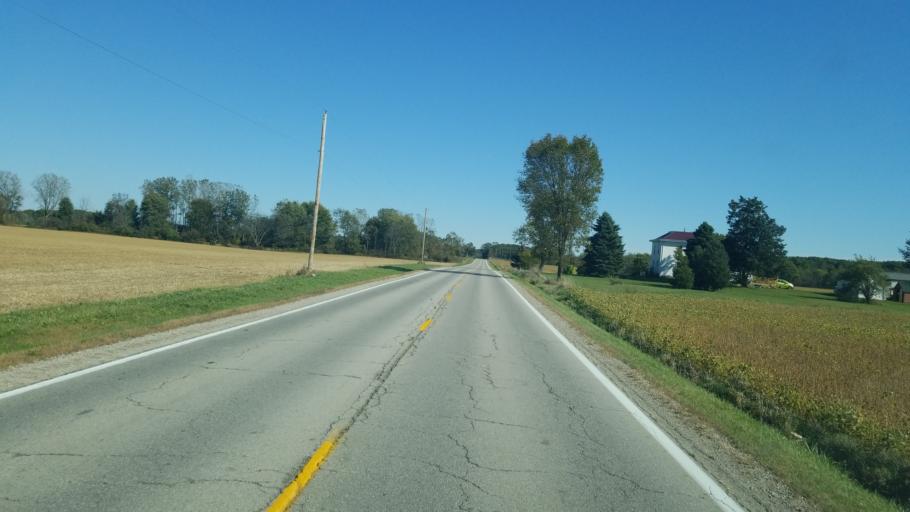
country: US
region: Ohio
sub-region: Huron County
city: New London
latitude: 41.0292
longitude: -82.4436
